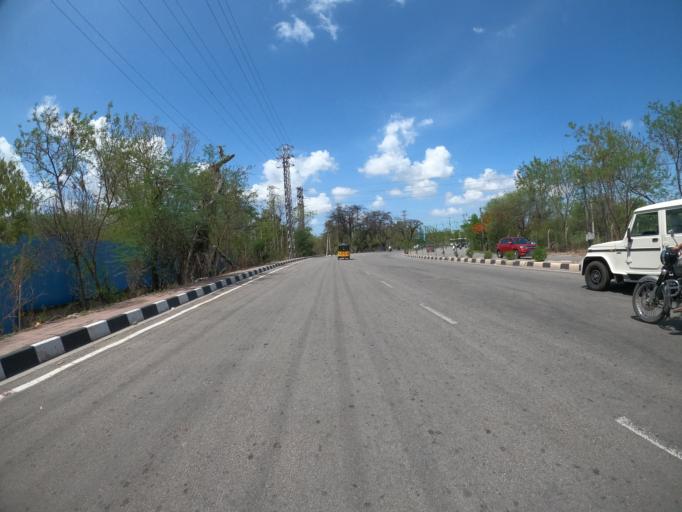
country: IN
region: Telangana
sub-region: Hyderabad
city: Hyderabad
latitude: 17.3693
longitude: 78.4039
